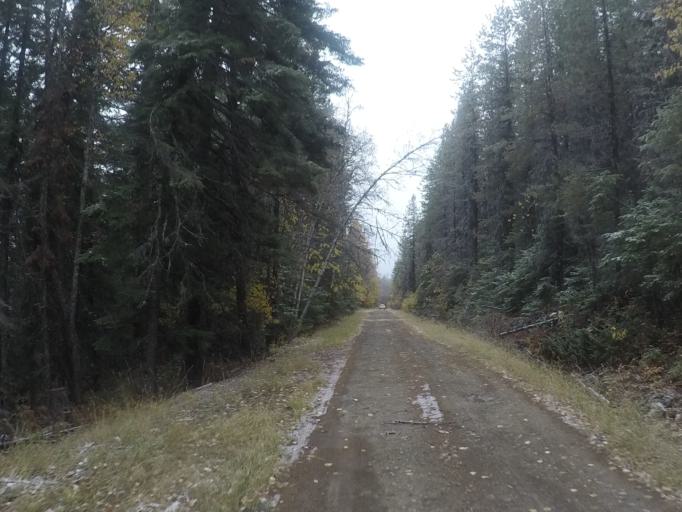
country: US
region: Montana
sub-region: Flathead County
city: Bigfork
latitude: 47.8855
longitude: -113.8757
